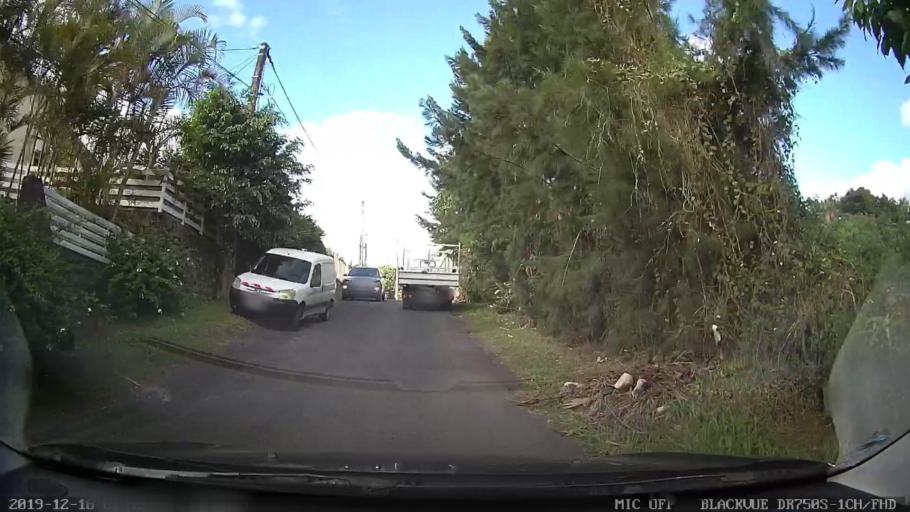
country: RE
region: Reunion
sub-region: Reunion
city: Le Tampon
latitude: -21.2489
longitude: 55.5186
